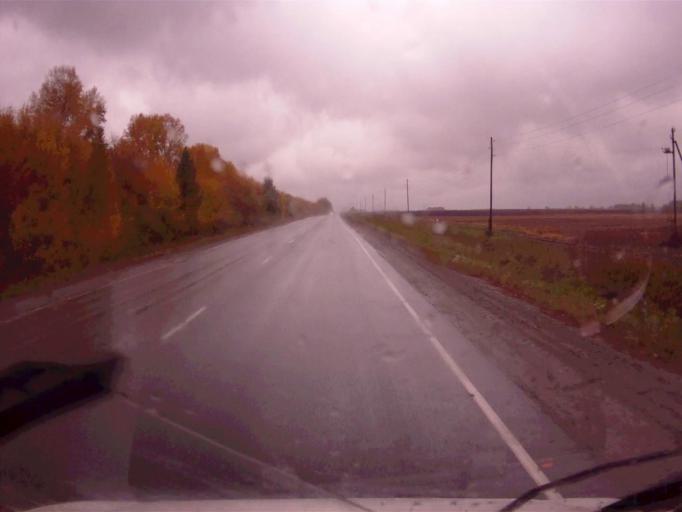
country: RU
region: Chelyabinsk
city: Argayash
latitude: 55.4254
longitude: 61.0039
